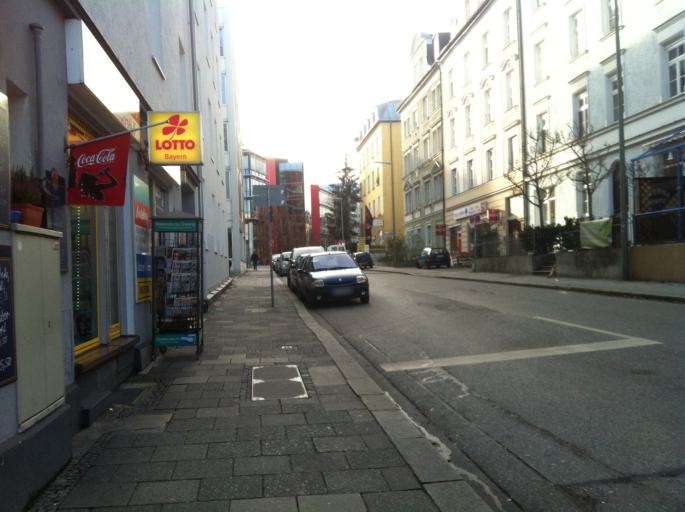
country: DE
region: Bavaria
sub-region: Upper Bavaria
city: Pullach im Isartal
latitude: 48.1002
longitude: 11.5332
